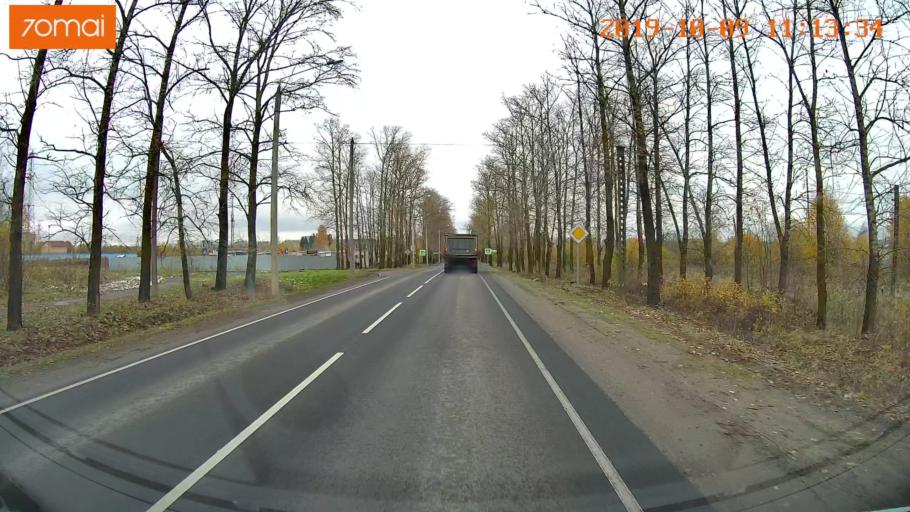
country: RU
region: Vologda
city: Vologda
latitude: 59.1828
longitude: 39.8447
